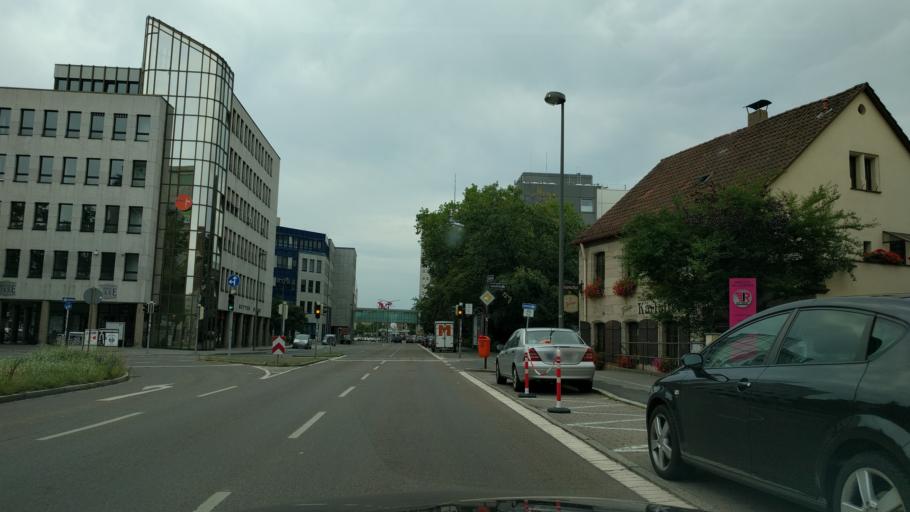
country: DE
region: Bavaria
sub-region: Regierungsbezirk Mittelfranken
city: Nuernberg
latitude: 49.4496
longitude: 11.0594
